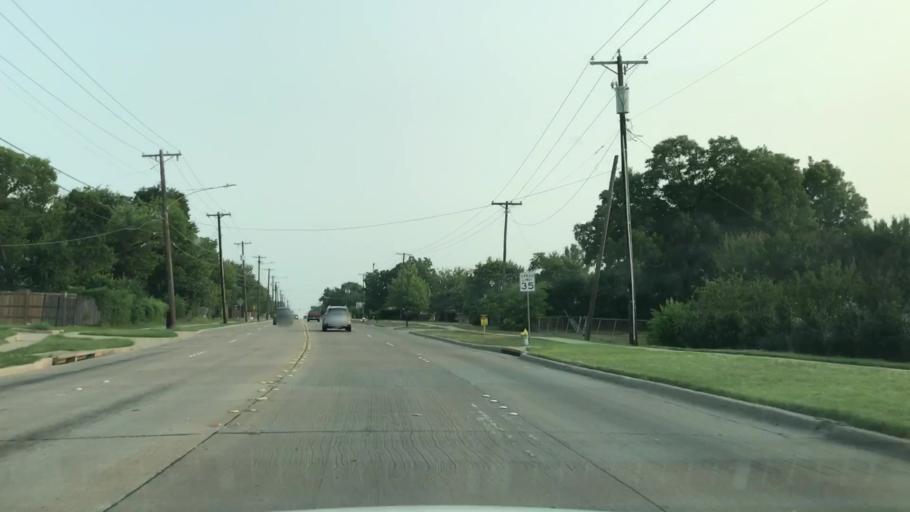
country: US
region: Texas
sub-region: Dallas County
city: Garland
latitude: 32.9017
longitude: -96.6222
